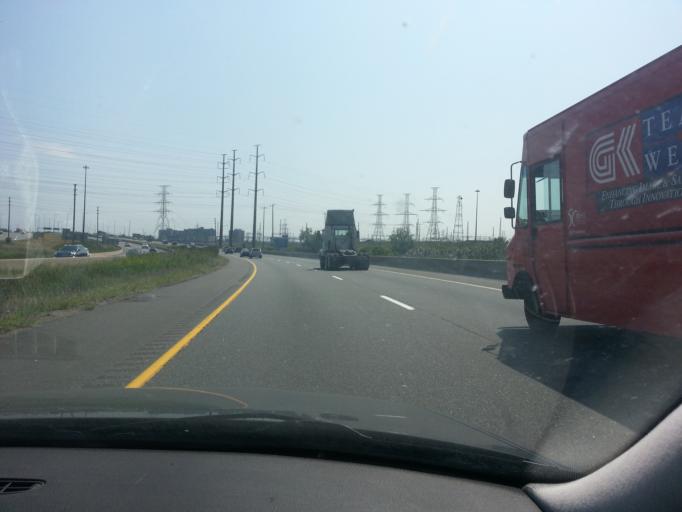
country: CA
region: Ontario
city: Burlington
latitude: 43.3361
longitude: -79.8293
